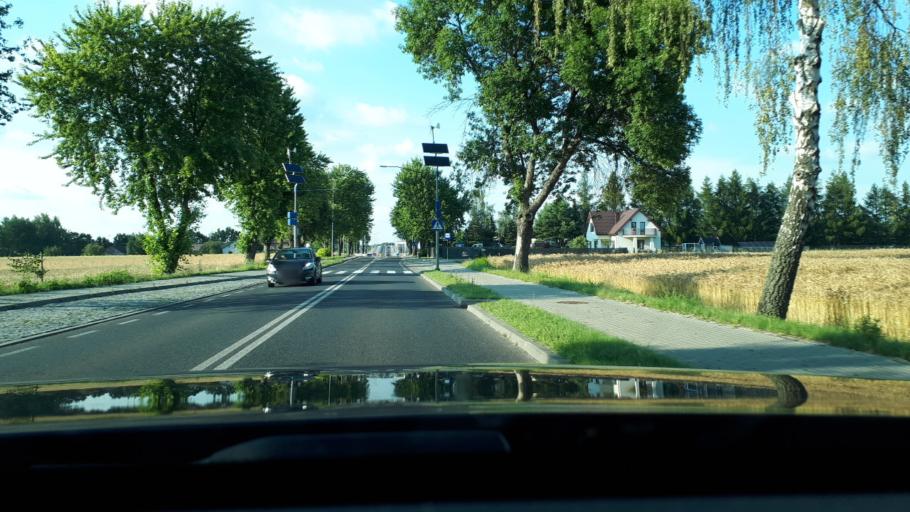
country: PL
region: Masovian Voivodeship
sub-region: Powiat ciechanowski
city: Ciechanow
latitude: 52.8485
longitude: 20.6237
